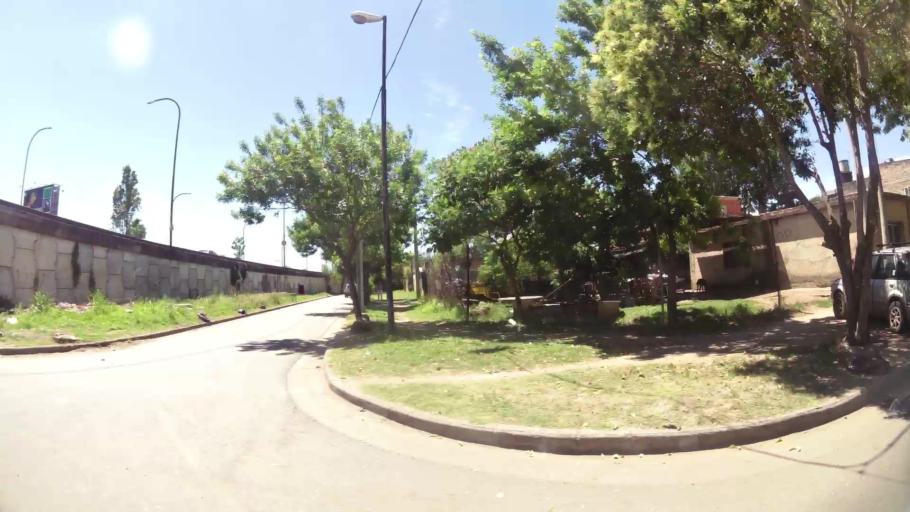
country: AR
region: Santa Fe
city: Perez
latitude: -32.9489
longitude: -60.7191
